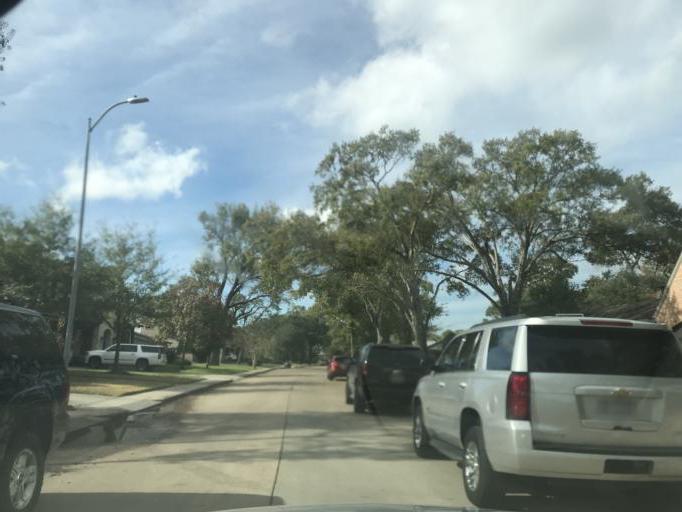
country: US
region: Texas
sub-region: Harris County
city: Hunters Creek Village
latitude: 29.7434
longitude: -95.4936
